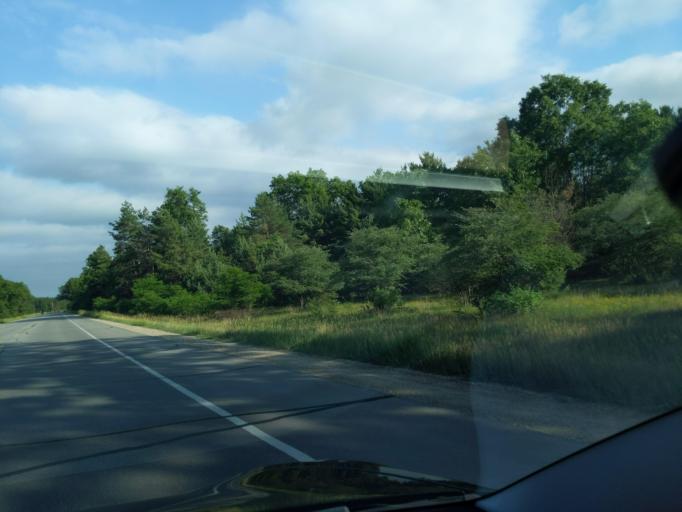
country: US
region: Michigan
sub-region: Muskegon County
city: Lakewood Club
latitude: 43.3905
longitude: -86.2959
